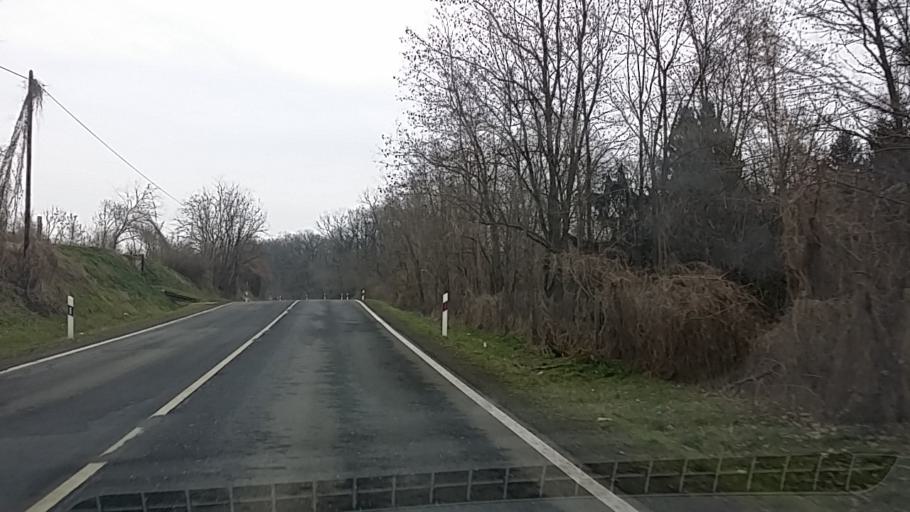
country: HU
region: Baranya
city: Dunaszekcso
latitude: 46.0584
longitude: 18.7301
